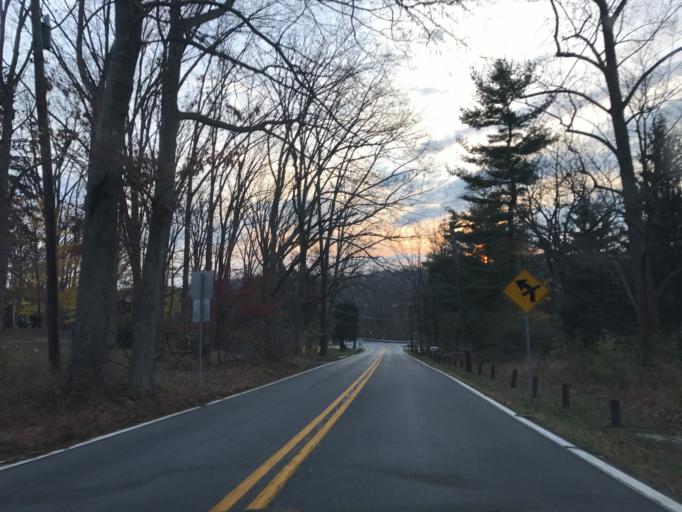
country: US
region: Maryland
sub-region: Frederick County
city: Braddock Heights
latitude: 39.4546
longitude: -77.4939
